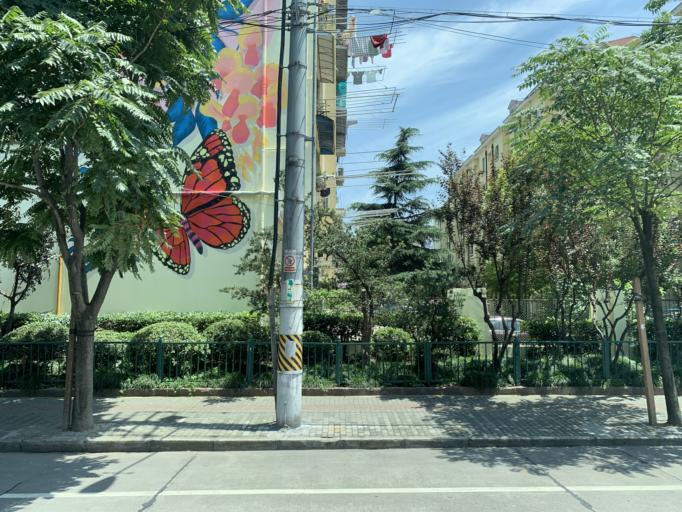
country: CN
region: Shanghai Shi
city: Pudong
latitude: 31.2498
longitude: 121.5747
